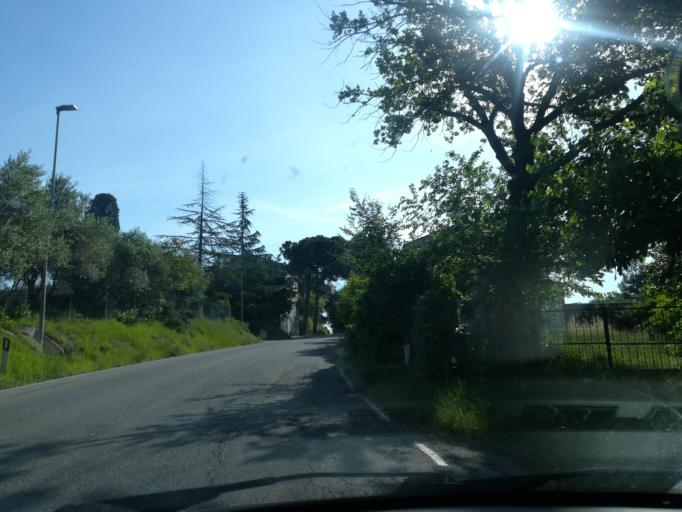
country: IT
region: The Marches
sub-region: Provincia di Macerata
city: Piediripa
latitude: 43.2952
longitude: 13.4769
